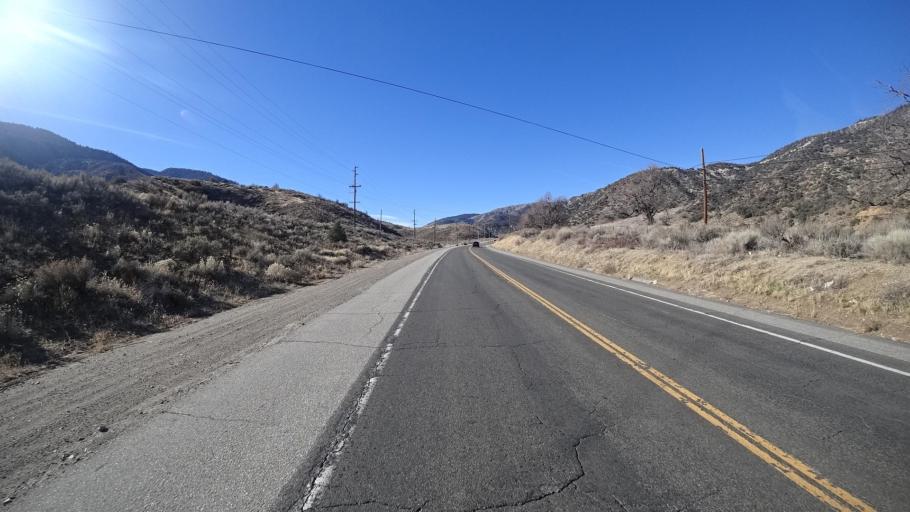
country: US
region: California
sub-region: Kern County
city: Frazier Park
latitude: 34.8185
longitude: -118.9129
